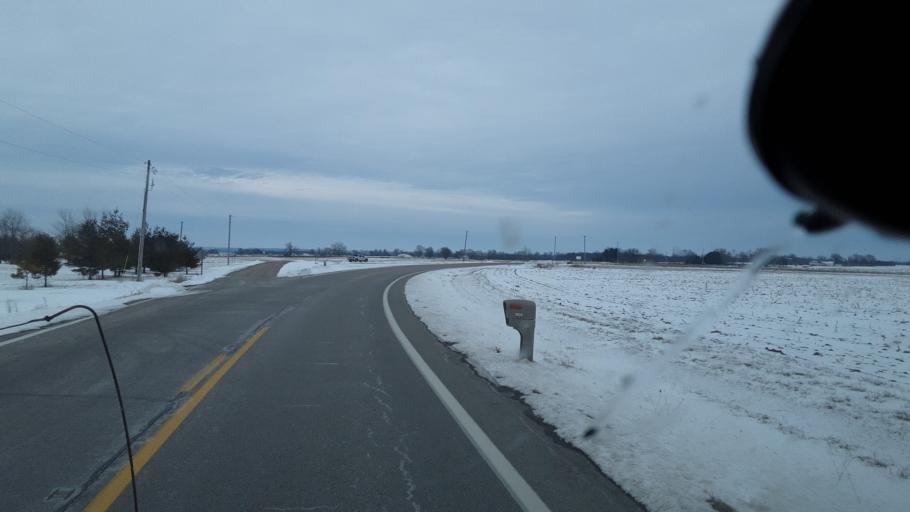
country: US
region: Ohio
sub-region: Pickaway County
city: Williamsport
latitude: 39.6306
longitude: -83.0598
